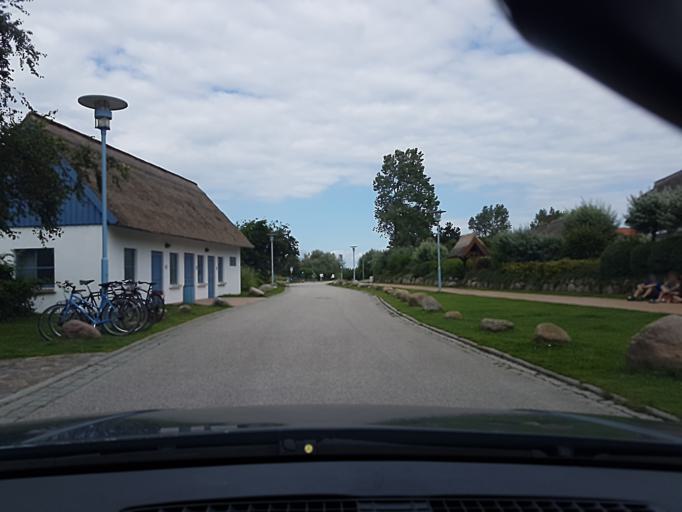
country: DE
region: Mecklenburg-Vorpommern
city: Ostseebad Dierhagen
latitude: 54.3519
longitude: 12.3878
